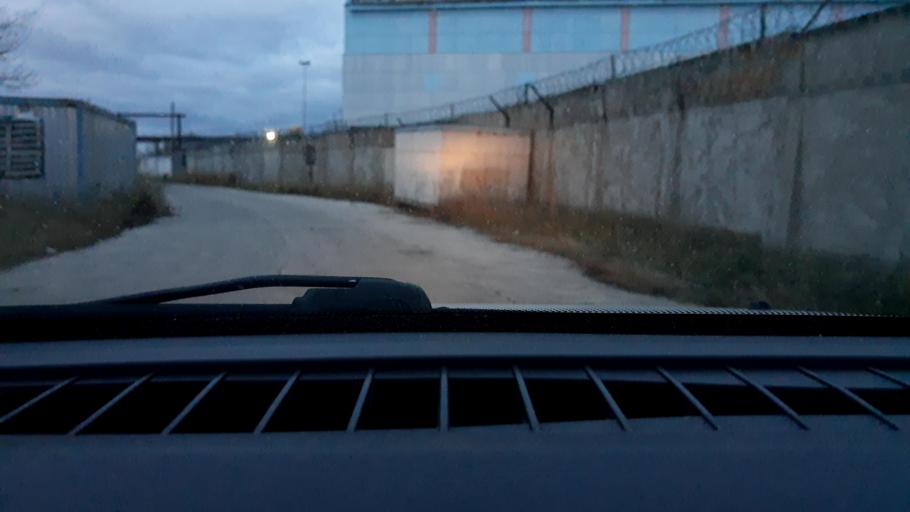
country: RU
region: Nizjnij Novgorod
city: Gorbatovka
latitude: 56.3630
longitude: 43.7899
